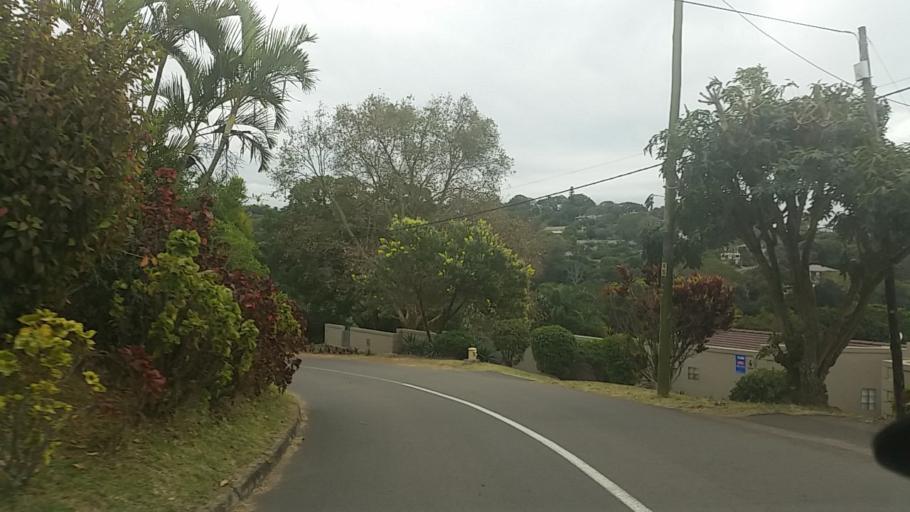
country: ZA
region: KwaZulu-Natal
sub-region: eThekwini Metropolitan Municipality
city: Berea
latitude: -29.8433
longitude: 30.9349
